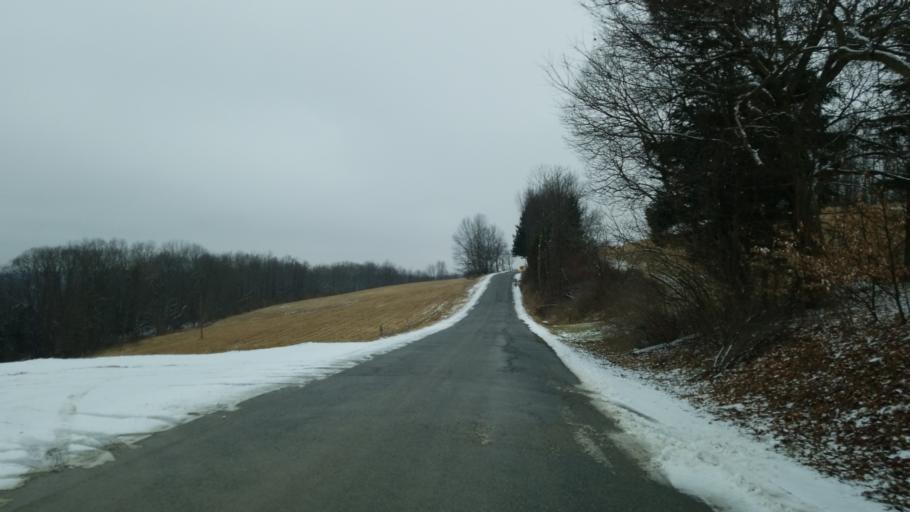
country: US
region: Pennsylvania
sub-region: Jefferson County
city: Sykesville
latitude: 41.0799
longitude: -78.8024
